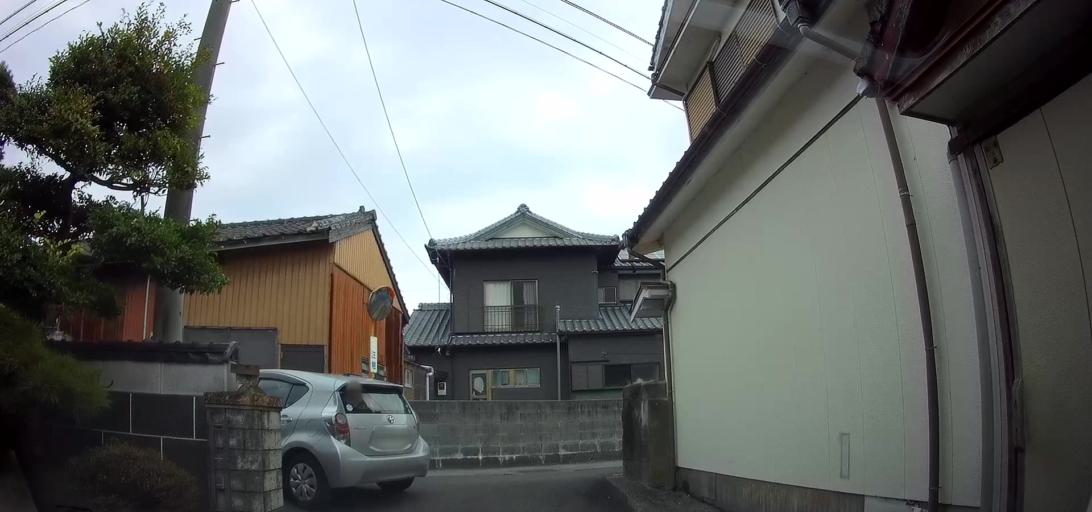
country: JP
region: Nagasaki
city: Shimabara
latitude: 32.6562
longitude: 130.3084
